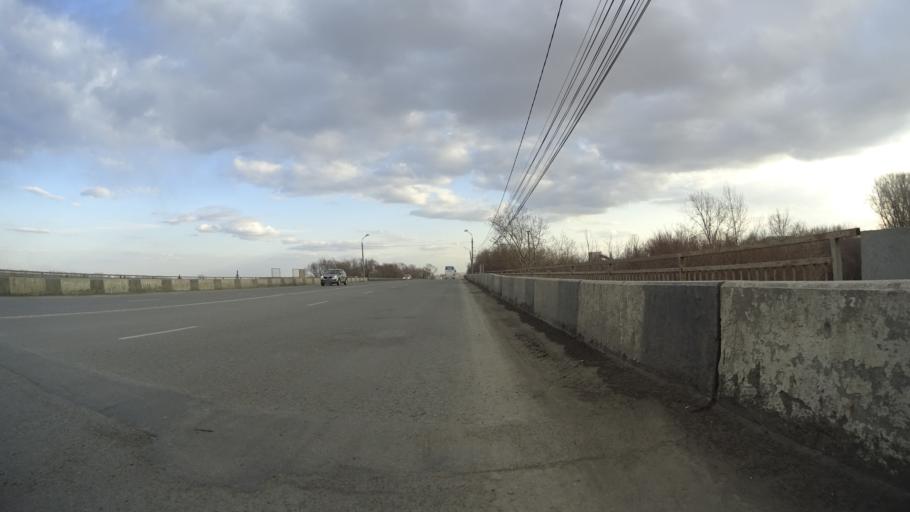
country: RU
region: Chelyabinsk
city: Novosineglazovskiy
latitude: 55.1024
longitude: 61.3875
